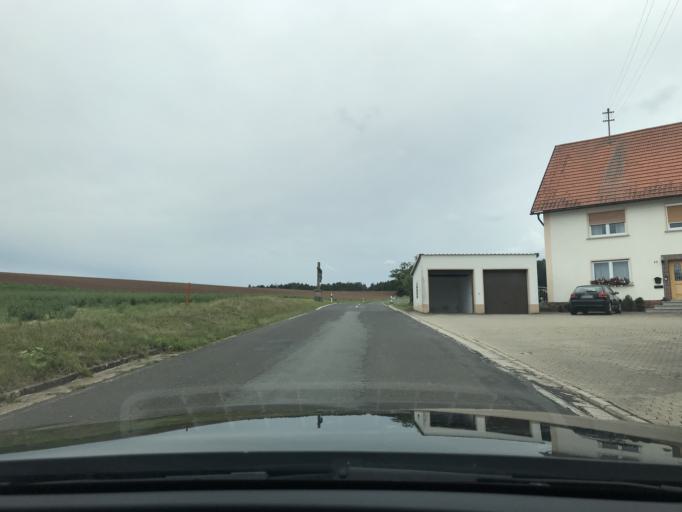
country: DE
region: Bavaria
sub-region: Regierungsbezirk Unterfranken
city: Burgpreppach
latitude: 50.1358
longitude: 10.6800
